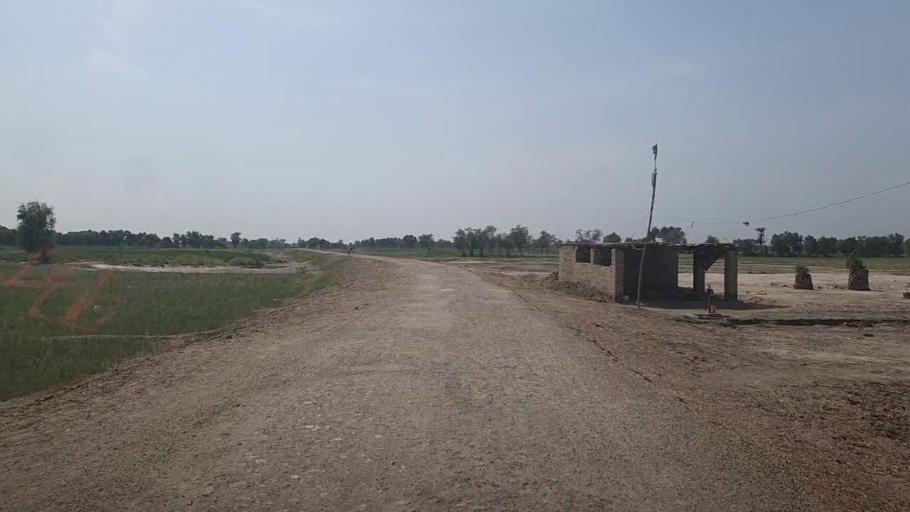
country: PK
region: Sindh
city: Ubauro
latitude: 28.1376
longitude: 69.8229
